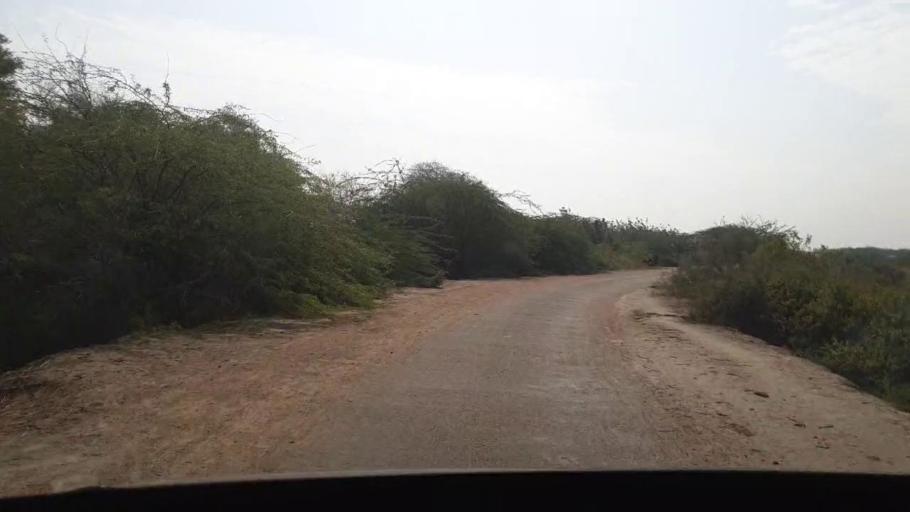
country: PK
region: Sindh
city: Chuhar Jamali
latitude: 24.2396
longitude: 67.9854
